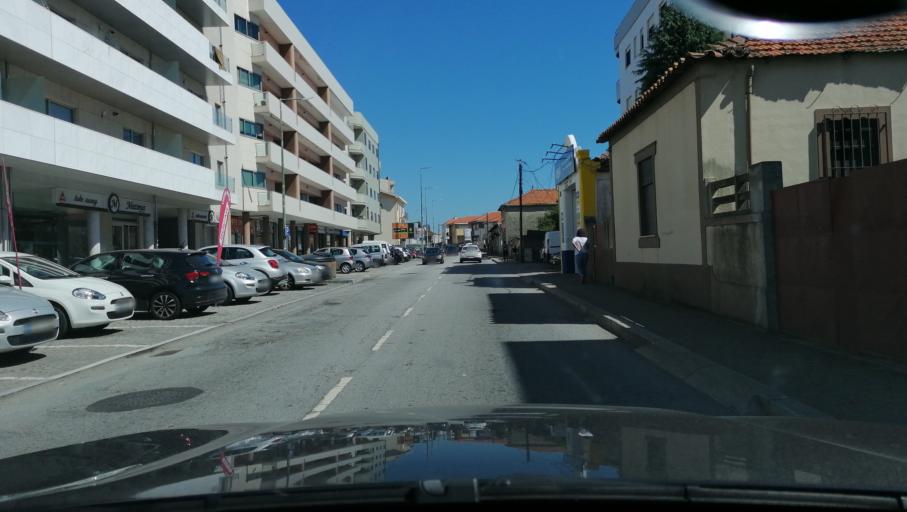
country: PT
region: Porto
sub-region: Vila Nova de Gaia
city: Canidelo
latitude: 41.1287
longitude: -8.6423
